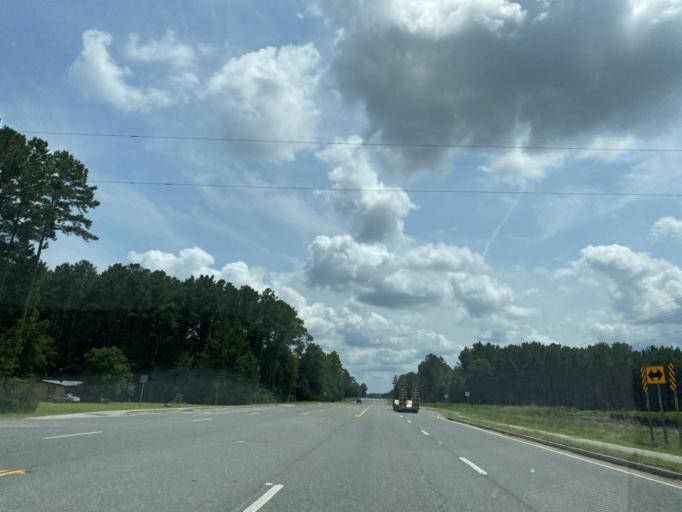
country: US
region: Georgia
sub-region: Ware County
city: Deenwood
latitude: 31.3475
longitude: -82.4638
